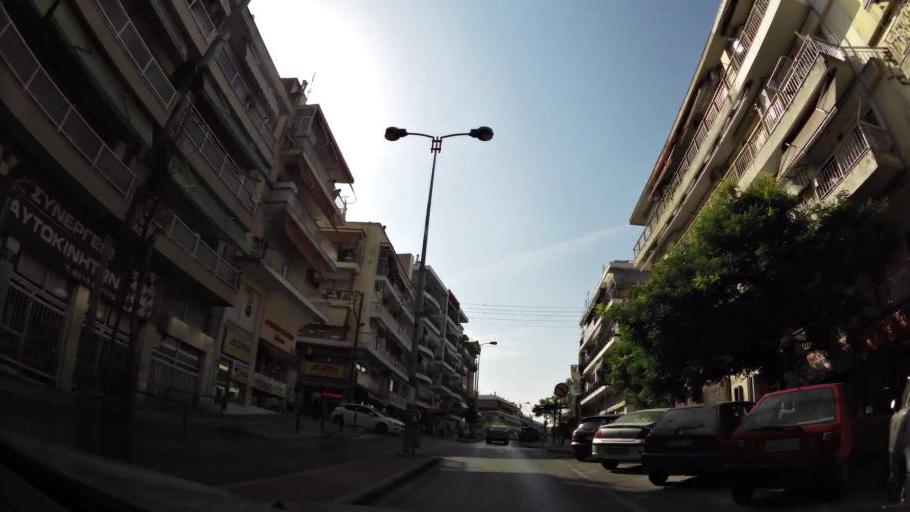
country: GR
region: Central Macedonia
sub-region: Nomos Thessalonikis
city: Agios Pavlos
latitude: 40.6398
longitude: 22.9514
